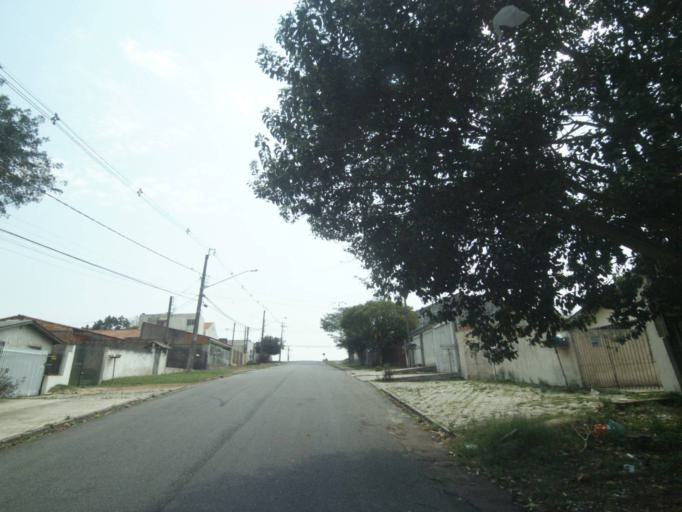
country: BR
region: Parana
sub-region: Sao Jose Dos Pinhais
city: Sao Jose dos Pinhais
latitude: -25.5370
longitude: -49.2459
